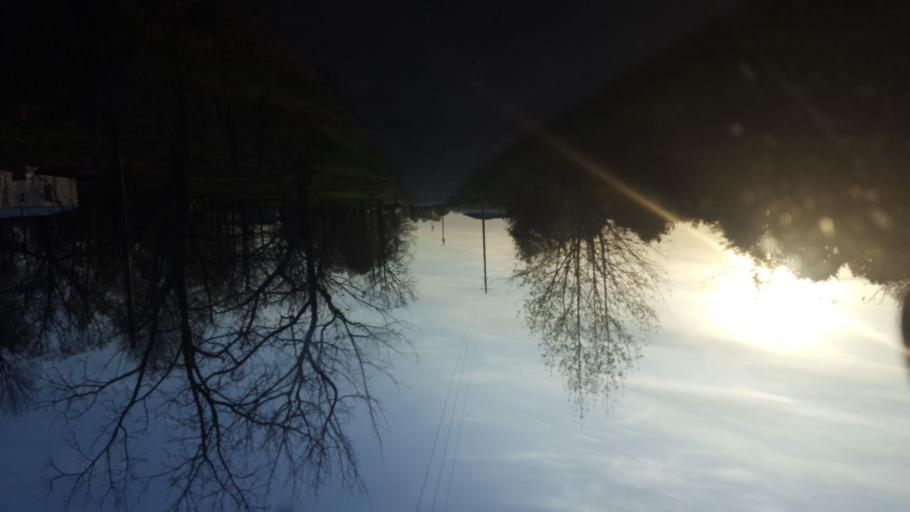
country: US
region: Kentucky
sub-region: Barren County
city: Cave City
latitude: 37.1730
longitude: -85.9930
